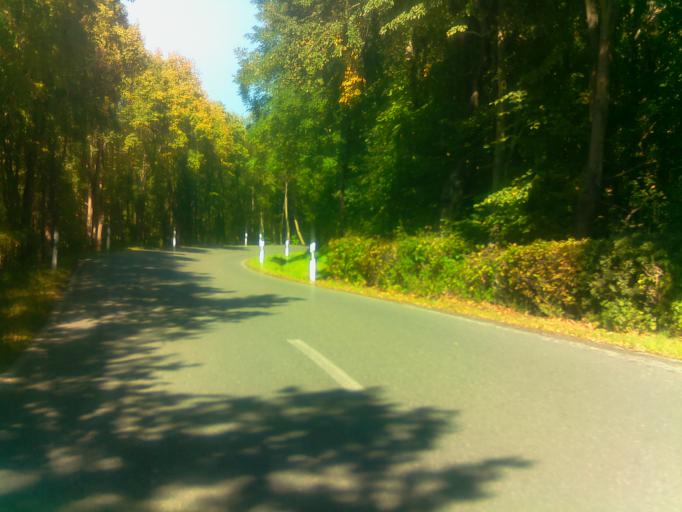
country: DE
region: Thuringia
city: Kahla
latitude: 50.8016
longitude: 11.5954
